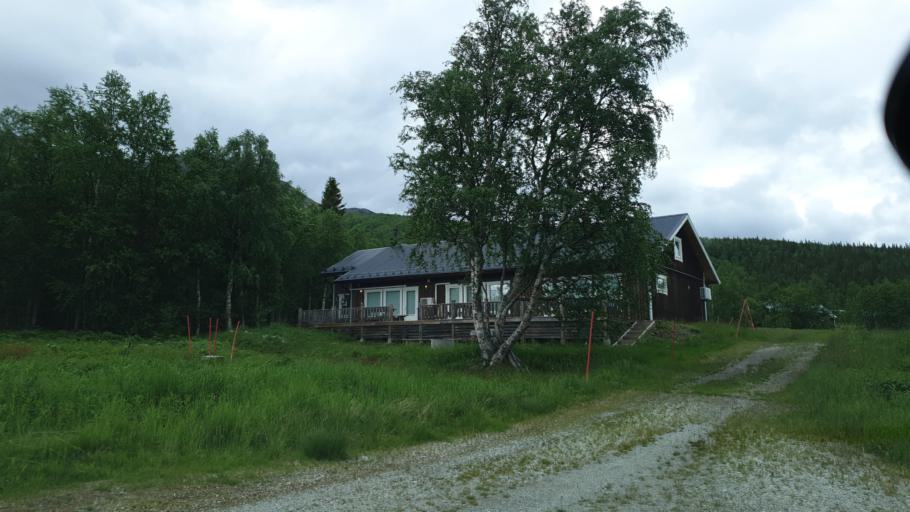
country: SE
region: Vaesterbotten
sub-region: Vilhelmina Kommun
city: Sjoberg
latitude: 65.2524
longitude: 15.5178
